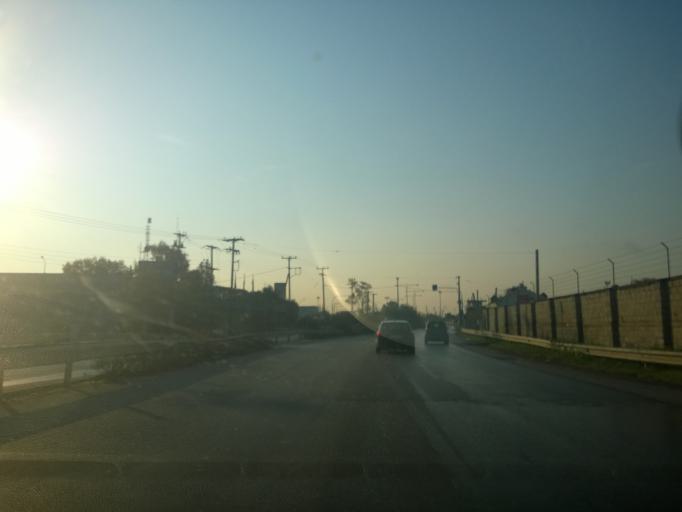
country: GR
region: Central Macedonia
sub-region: Nomos Thessalonikis
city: Menemeni
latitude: 40.6511
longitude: 22.9017
